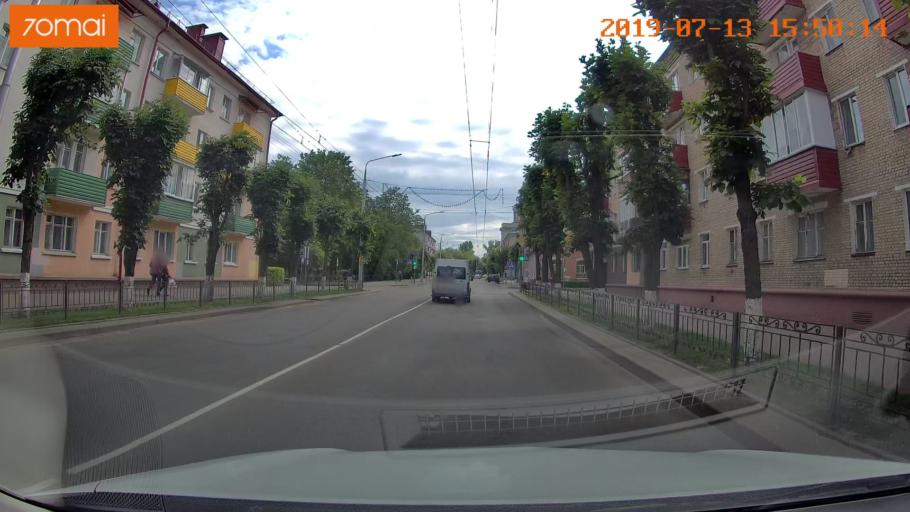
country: BY
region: Mogilev
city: Babruysk
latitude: 53.1439
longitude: 29.2260
